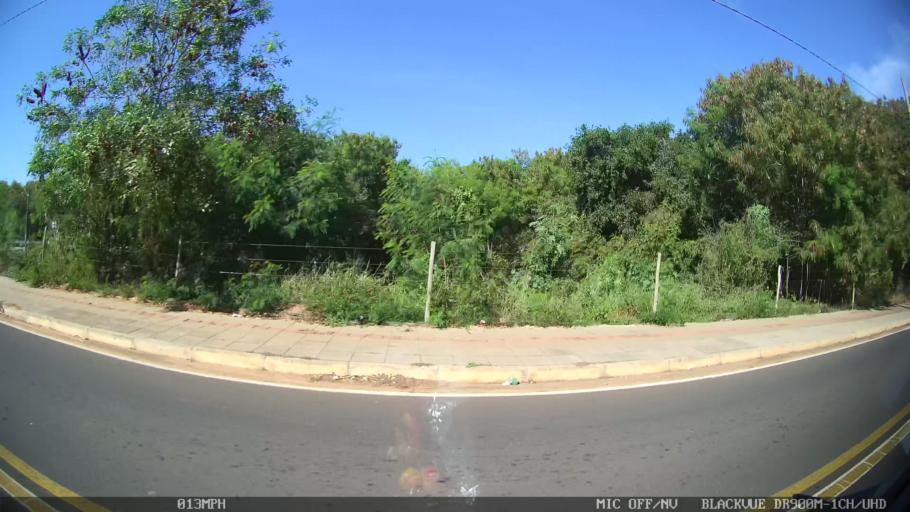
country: BR
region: Sao Paulo
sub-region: Sao Jose Do Rio Preto
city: Sao Jose do Rio Preto
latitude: -20.7778
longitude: -49.3830
